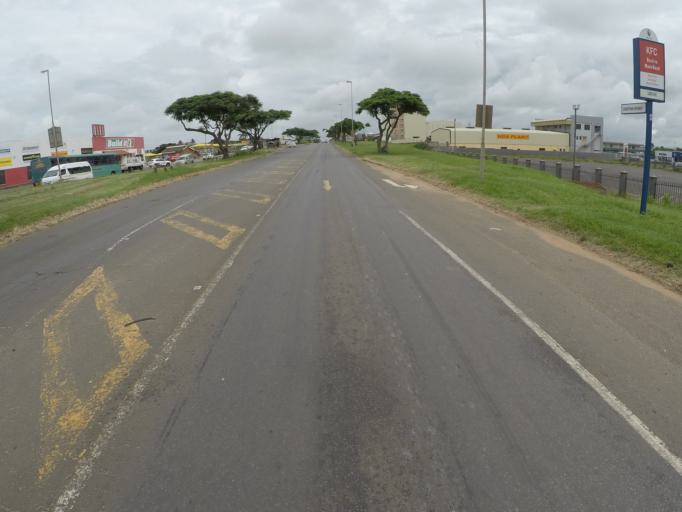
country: ZA
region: KwaZulu-Natal
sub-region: uThungulu District Municipality
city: Empangeni
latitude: -28.7746
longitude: 31.9010
